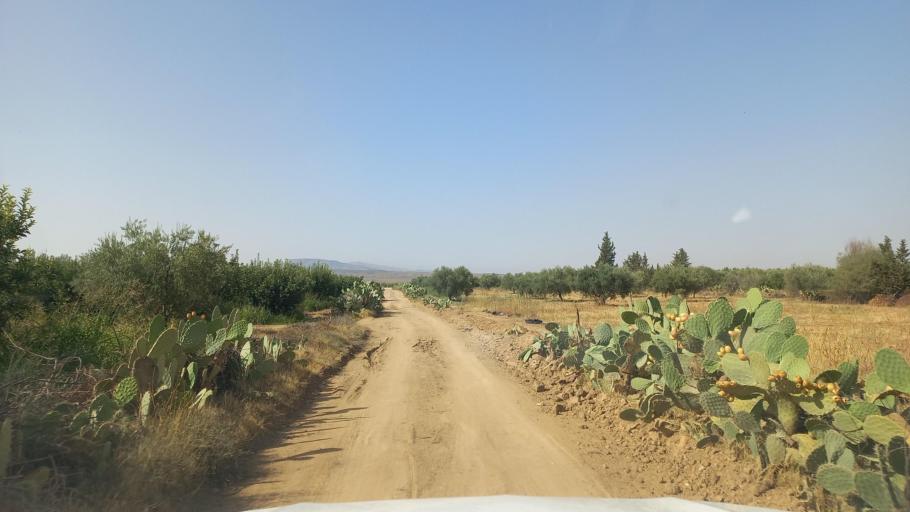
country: TN
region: Al Qasrayn
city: Kasserine
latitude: 35.2447
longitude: 9.0296
